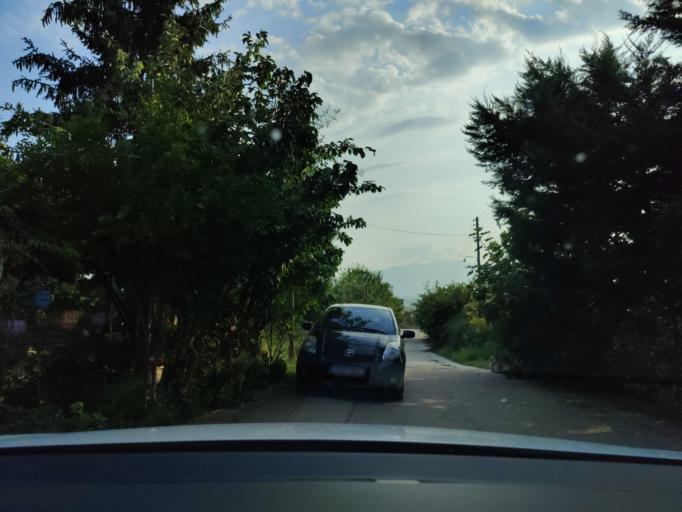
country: GR
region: East Macedonia and Thrace
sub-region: Nomos Kavalas
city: Zygos
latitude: 41.0184
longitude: 24.3850
